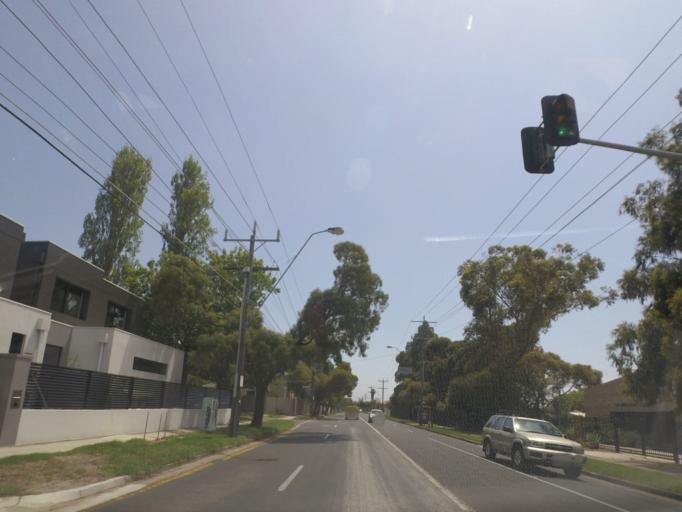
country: AU
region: Victoria
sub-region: Bayside
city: Hampton East
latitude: -37.9512
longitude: 145.0212
